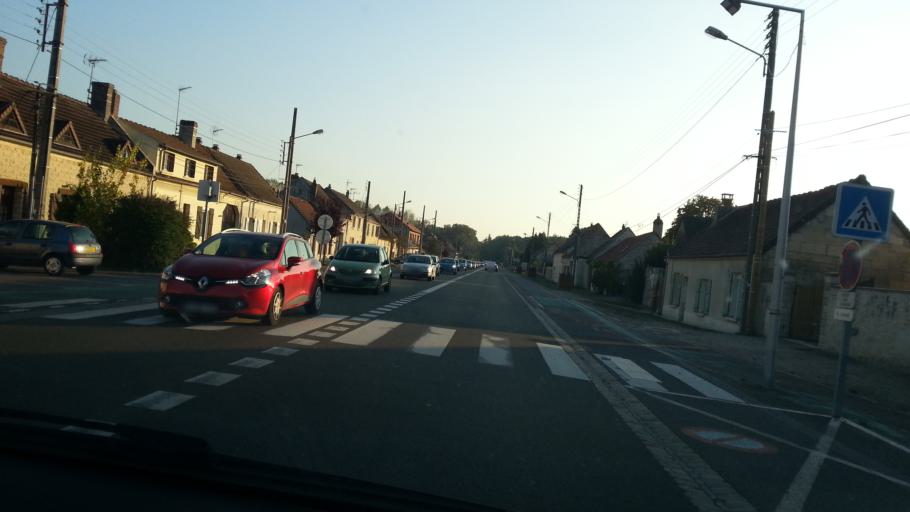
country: FR
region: Picardie
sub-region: Departement de l'Oise
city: Saint-Martin-Longueau
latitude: 49.3376
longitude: 2.6048
